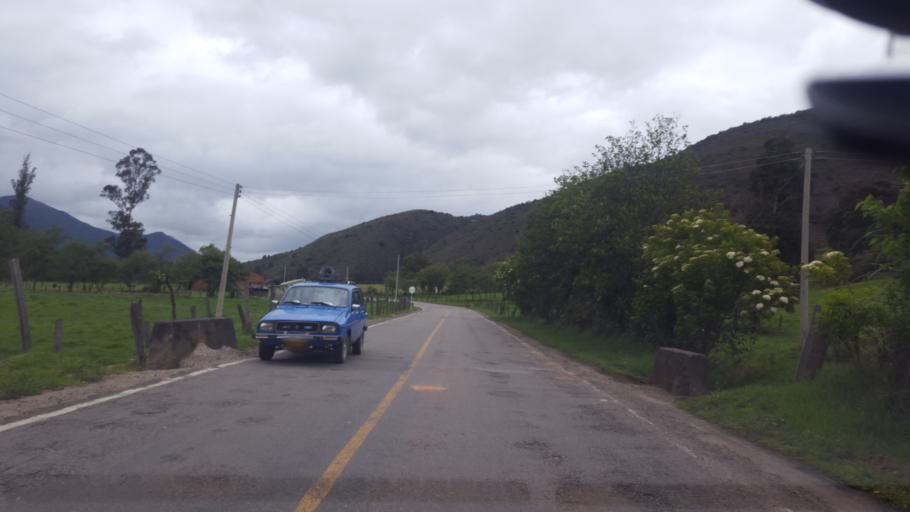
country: CO
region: Boyaca
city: Belen
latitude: 6.0122
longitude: -72.8282
